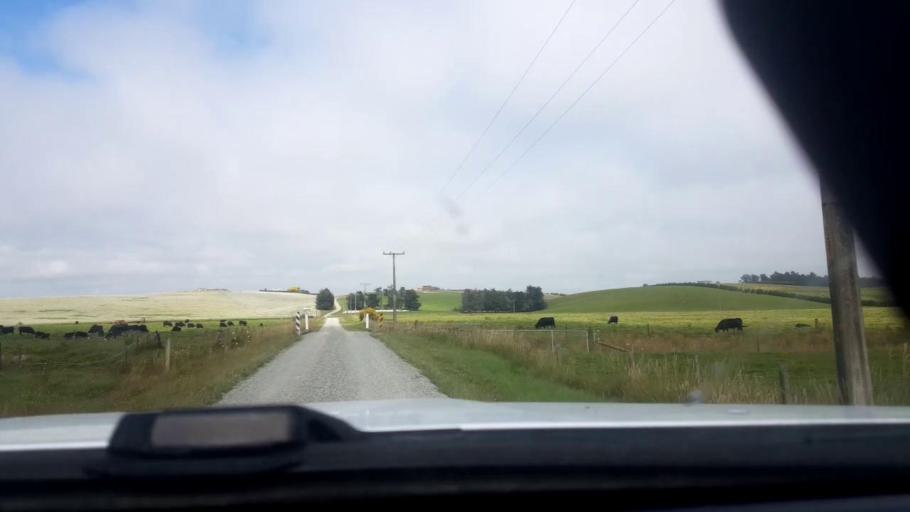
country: NZ
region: Canterbury
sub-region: Timaru District
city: Timaru
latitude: -44.3287
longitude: 171.2041
